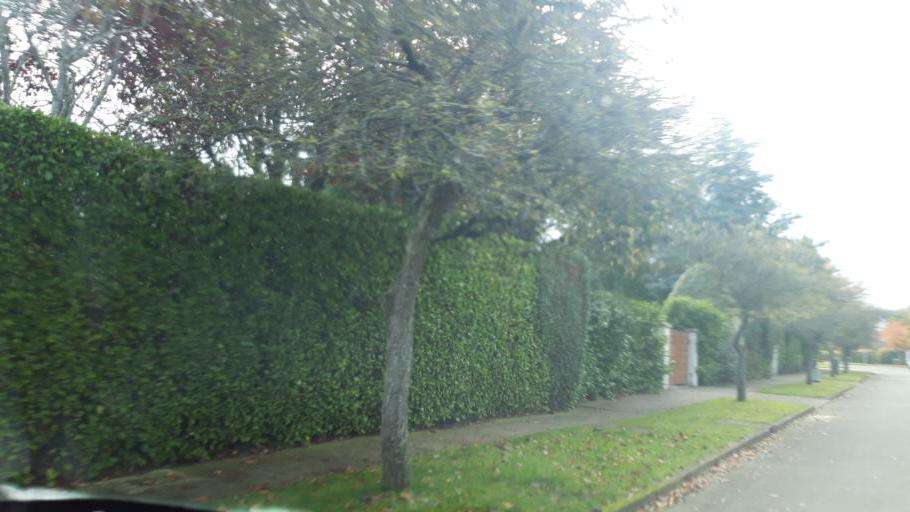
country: IE
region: Leinster
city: Mount Merrion
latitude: 53.3000
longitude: -6.2292
